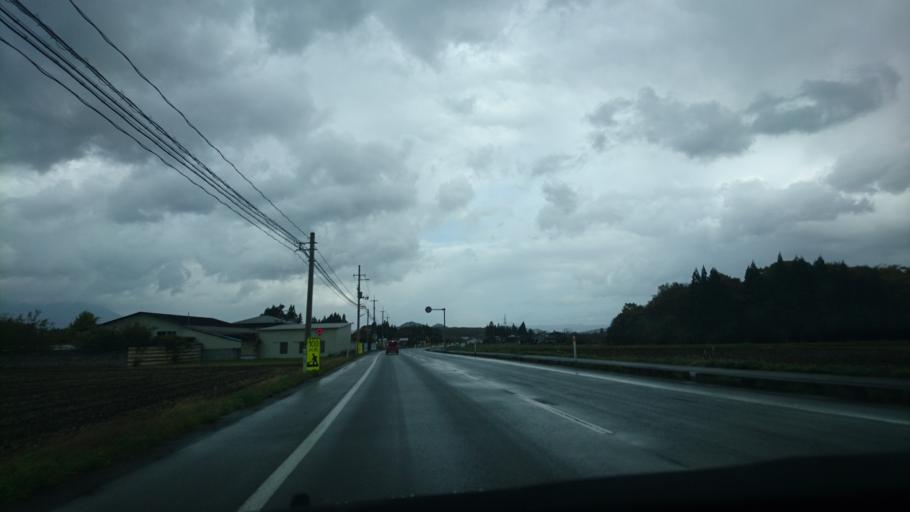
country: JP
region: Iwate
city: Shizukuishi
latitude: 39.6575
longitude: 140.9606
